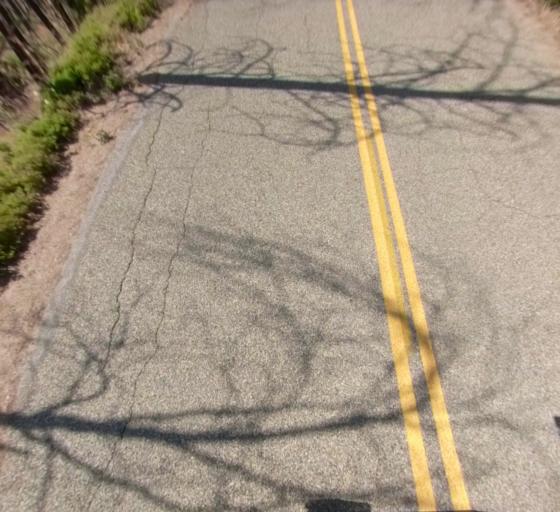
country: US
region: California
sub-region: Fresno County
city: Auberry
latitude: 37.2745
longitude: -119.3578
